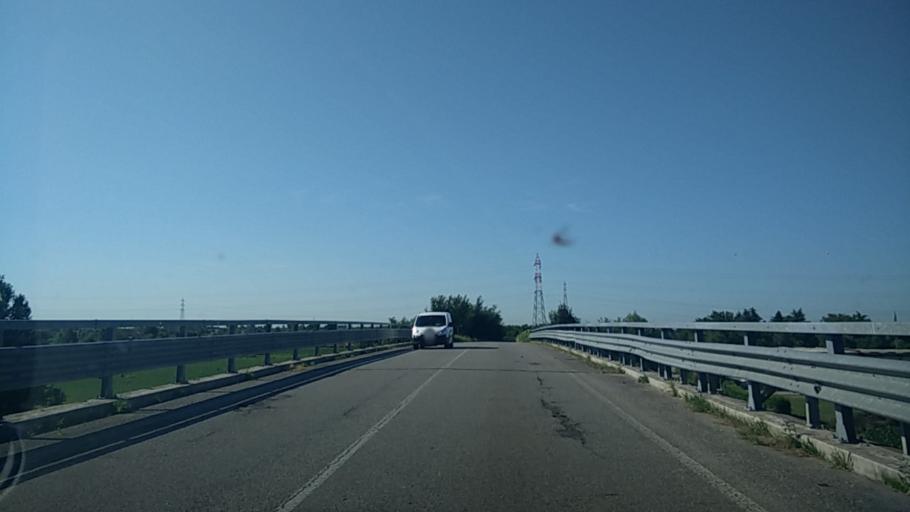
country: IT
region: Veneto
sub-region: Provincia di Venezia
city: Dolo
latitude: 45.4051
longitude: 12.0831
